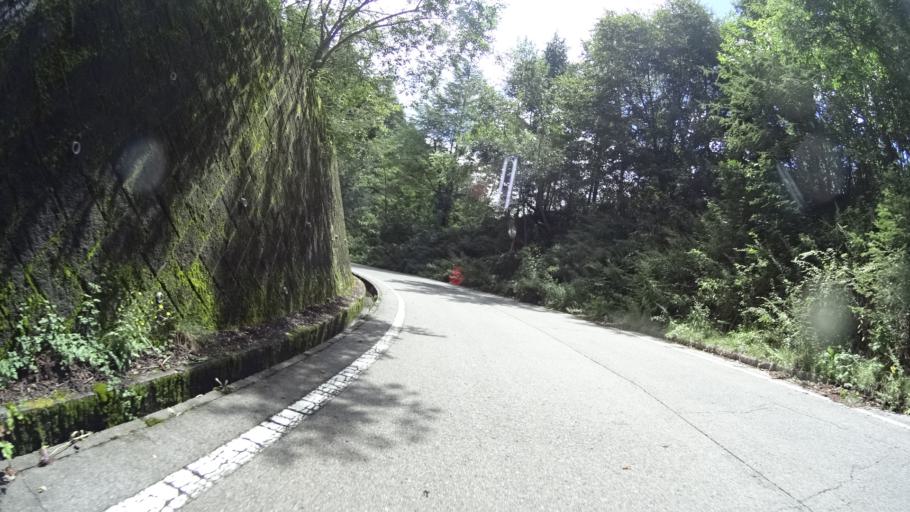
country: JP
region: Yamanashi
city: Enzan
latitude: 35.7162
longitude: 138.8363
